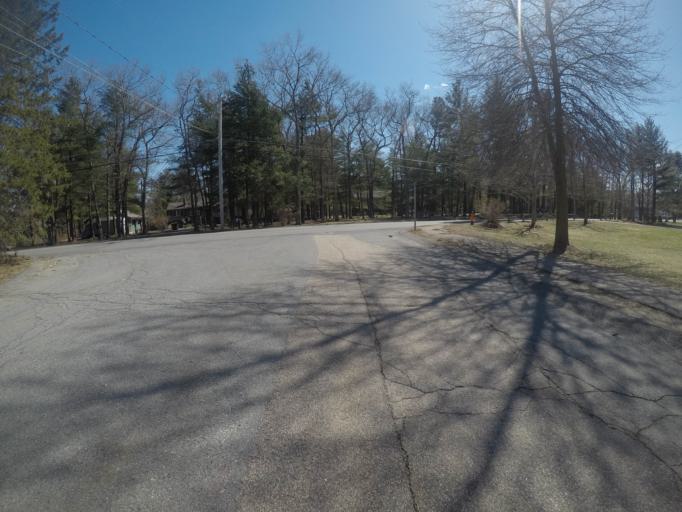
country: US
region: Massachusetts
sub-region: Bristol County
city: Easton
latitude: 41.9987
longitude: -71.1201
